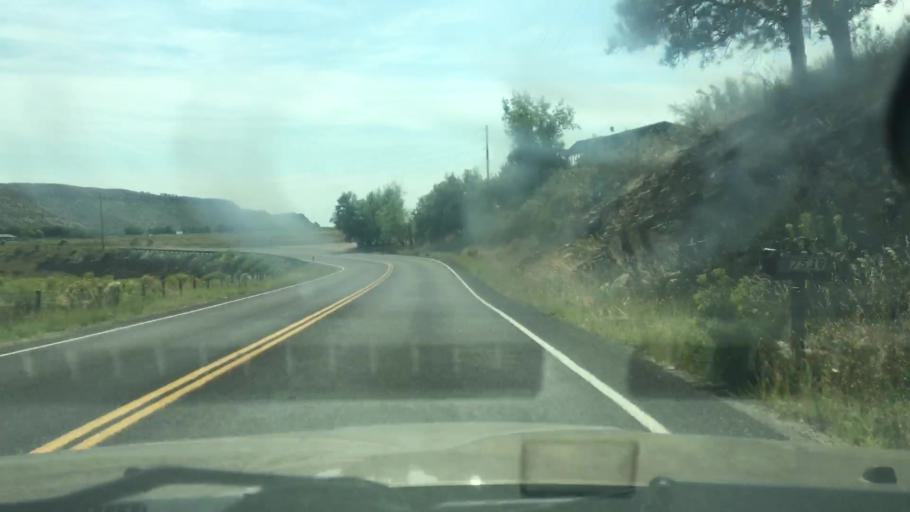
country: US
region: Colorado
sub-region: Larimer County
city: Loveland
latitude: 40.4701
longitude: -105.2111
